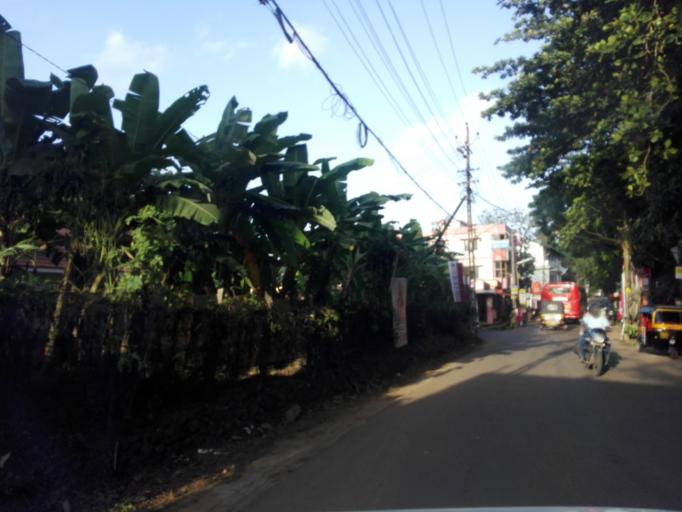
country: IN
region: Kerala
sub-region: Kottayam
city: Kottayam
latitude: 9.6124
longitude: 76.4974
